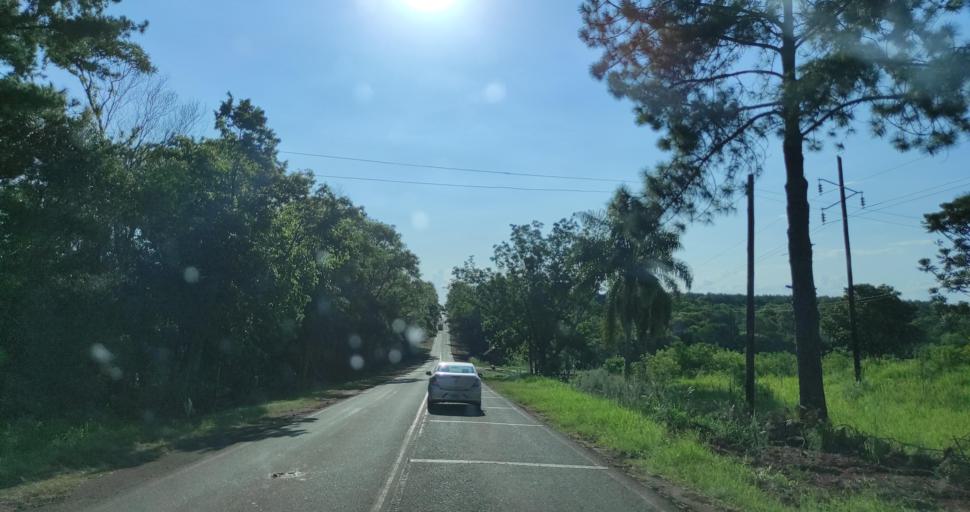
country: AR
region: Misiones
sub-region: Departamento de Eldorado
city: Eldorado
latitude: -26.3997
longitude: -54.3880
